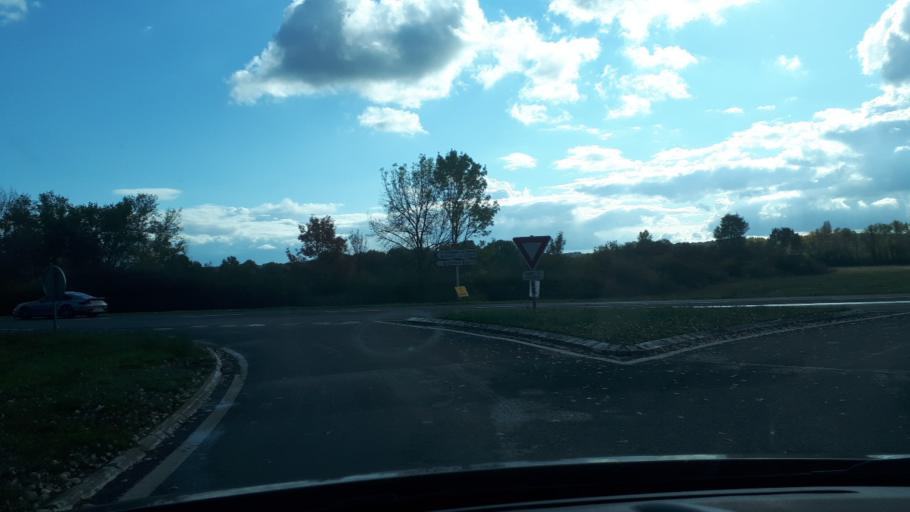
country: FR
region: Centre
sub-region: Departement du Loir-et-Cher
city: Mareuil-sur-Cher
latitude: 47.3091
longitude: 1.3390
